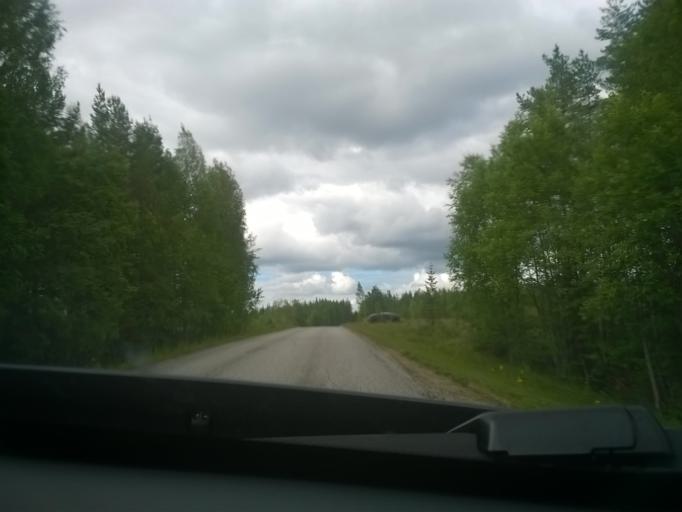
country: FI
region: Kainuu
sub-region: Kehys-Kainuu
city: Kuhmo
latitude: 64.3945
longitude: 29.7813
